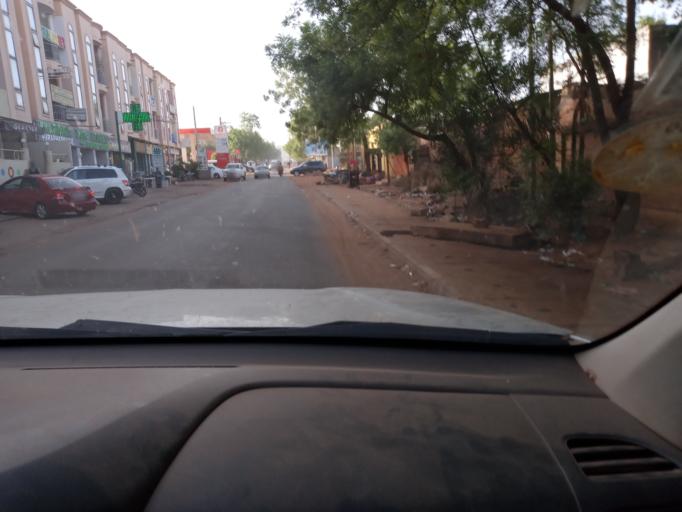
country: ML
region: Bamako
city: Bamako
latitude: 12.6604
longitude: -7.9721
